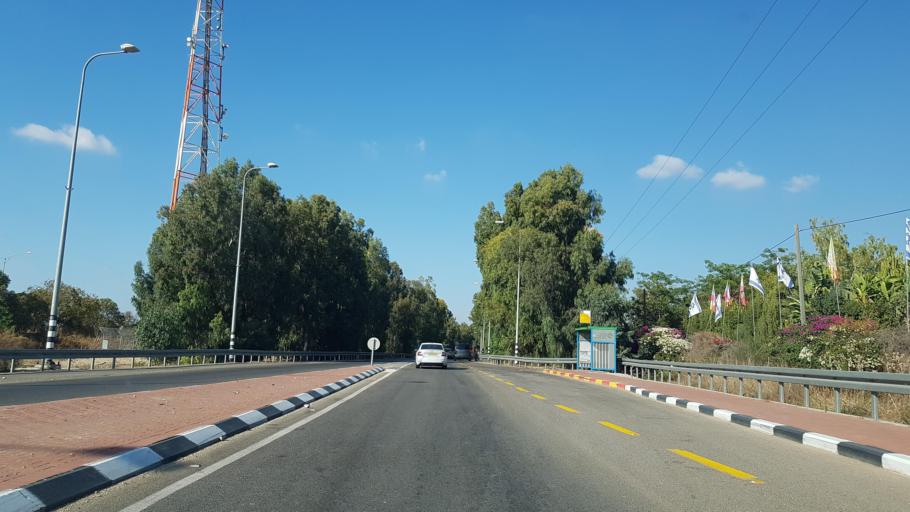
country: PS
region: West Bank
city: Tulkarm
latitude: 32.3512
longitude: 35.0138
